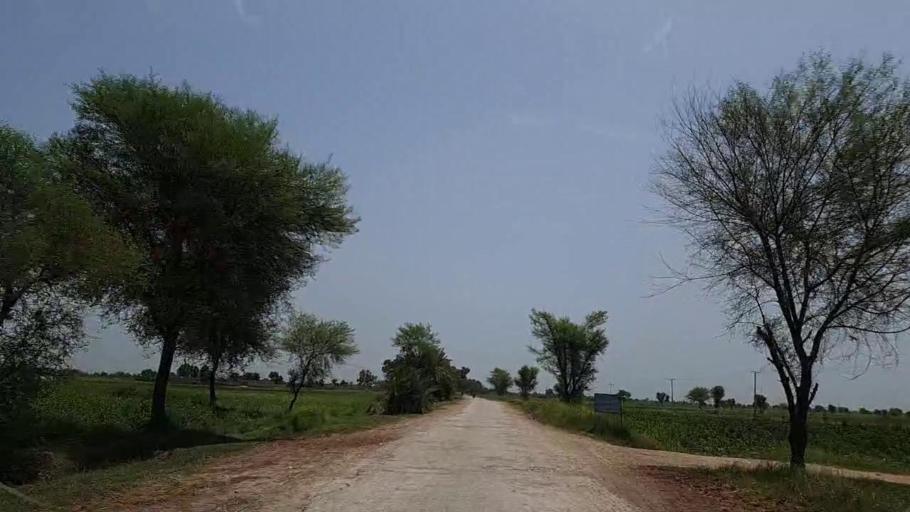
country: PK
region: Sindh
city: Tharu Shah
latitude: 26.9639
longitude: 68.0535
